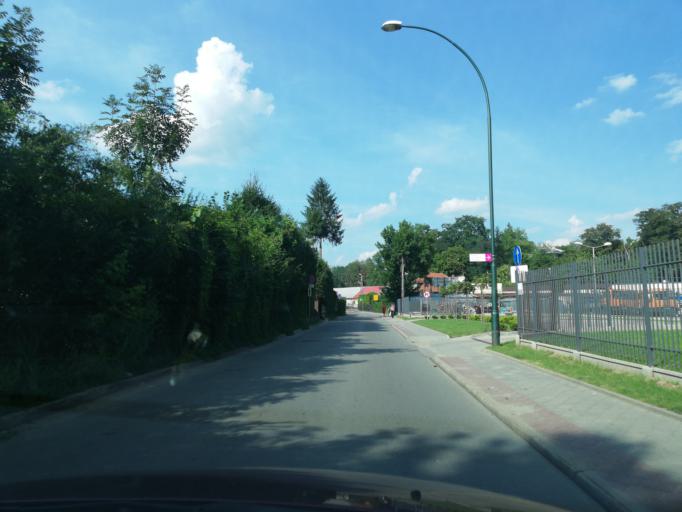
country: PL
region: Lesser Poland Voivodeship
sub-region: Powiat nowosadecki
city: Nowy Sacz
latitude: 49.6172
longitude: 20.6911
